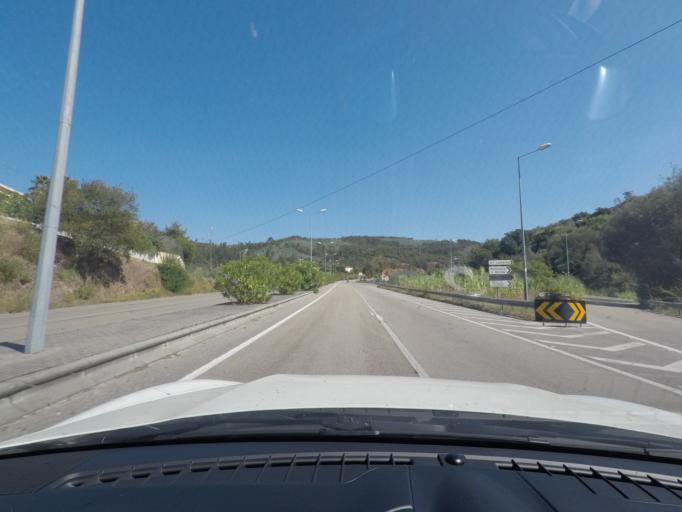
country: PT
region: Coimbra
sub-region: Coimbra
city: Coimbra
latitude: 40.2238
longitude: -8.4021
